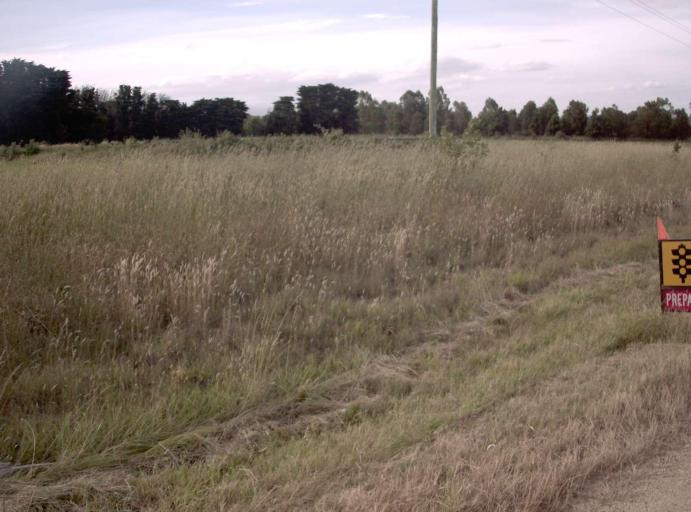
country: AU
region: Victoria
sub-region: Wellington
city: Heyfield
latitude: -38.0054
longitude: 146.7804
